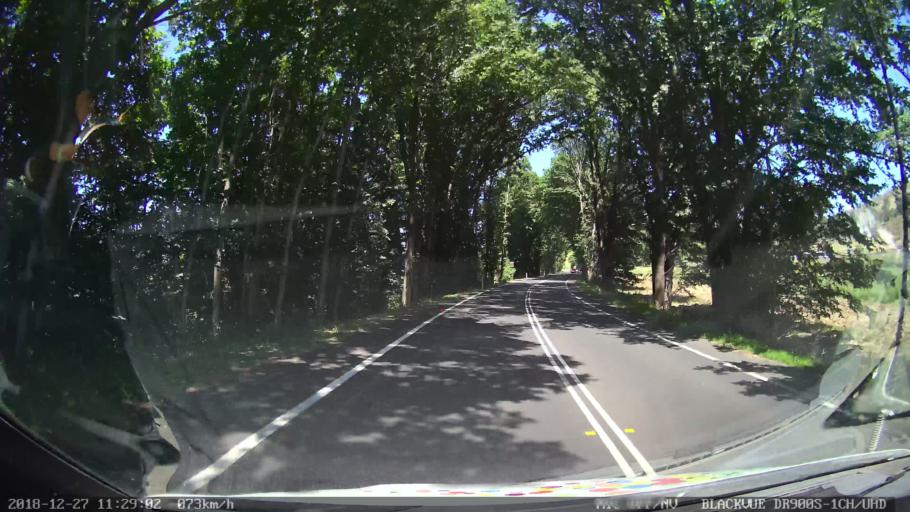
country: AU
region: New South Wales
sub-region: Bathurst Regional
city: Perthville
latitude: -33.4824
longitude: 149.5573
